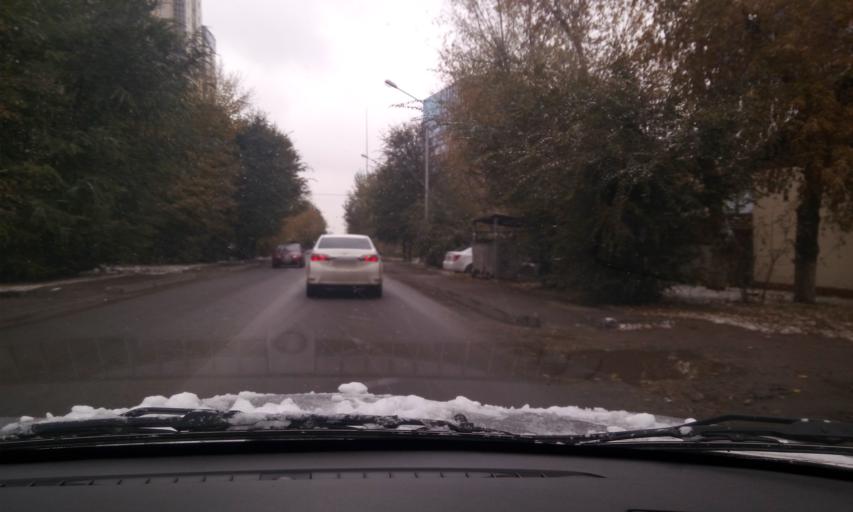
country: KZ
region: Astana Qalasy
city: Astana
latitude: 51.1452
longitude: 71.4267
